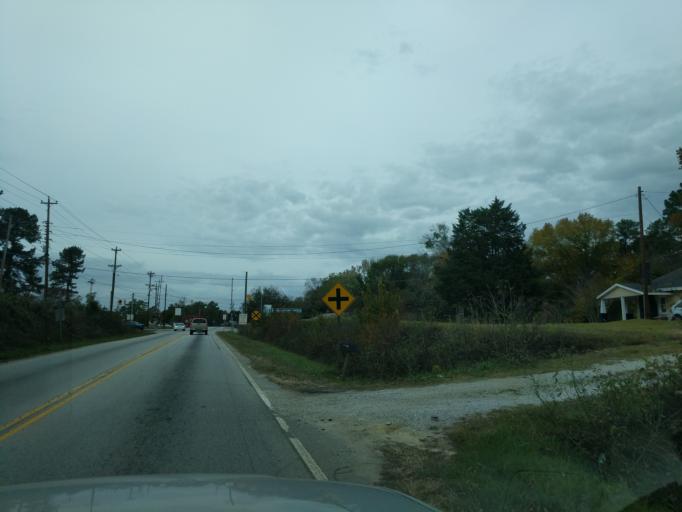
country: US
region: South Carolina
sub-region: Newberry County
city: Newberry
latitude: 34.2809
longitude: -81.6368
